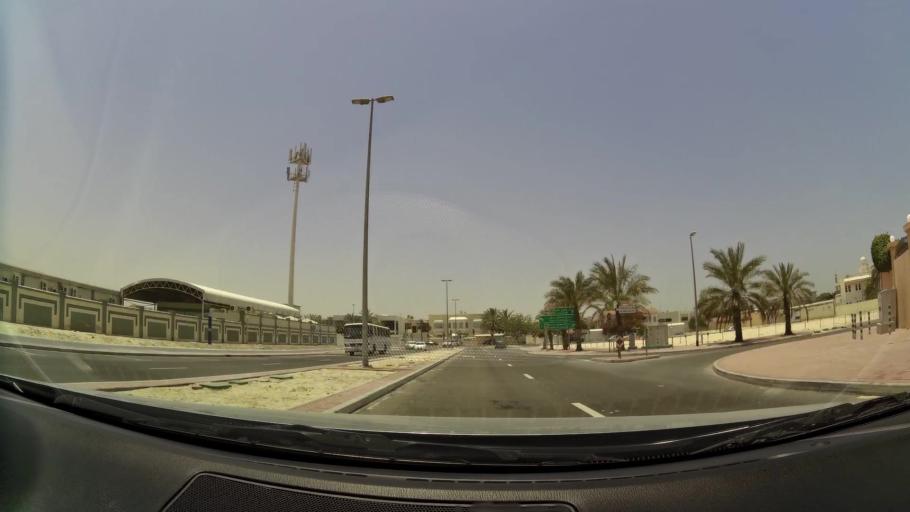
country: AE
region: Dubai
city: Dubai
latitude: 25.1858
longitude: 55.2325
